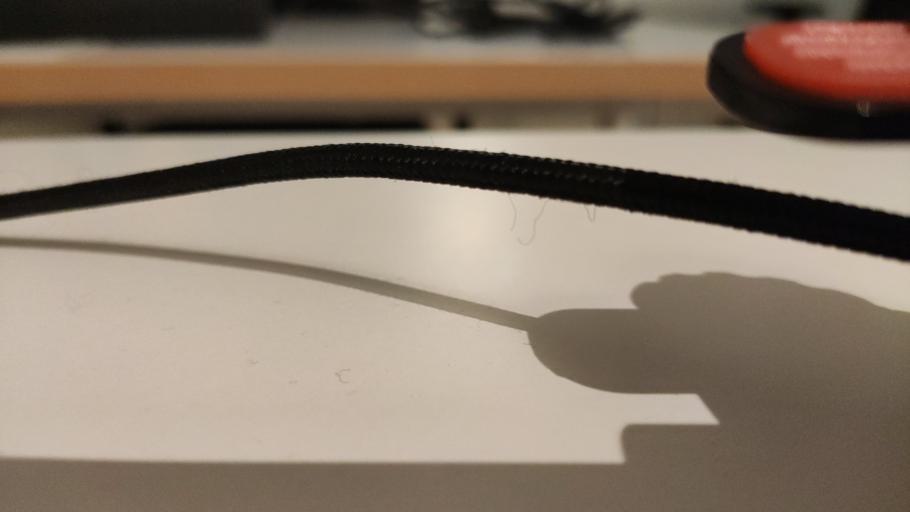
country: RU
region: Moskovskaya
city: Gorshkovo
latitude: 56.3746
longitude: 37.4087
